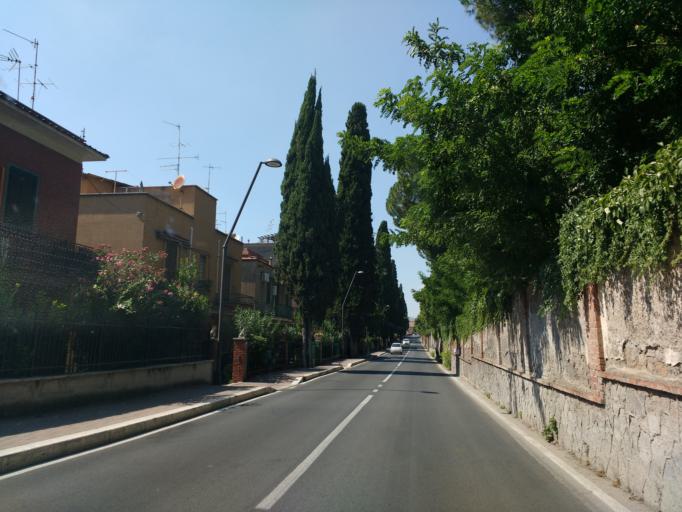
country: IT
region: Latium
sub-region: Citta metropolitana di Roma Capitale
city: Villa Adriana
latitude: 41.9542
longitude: 12.7766
